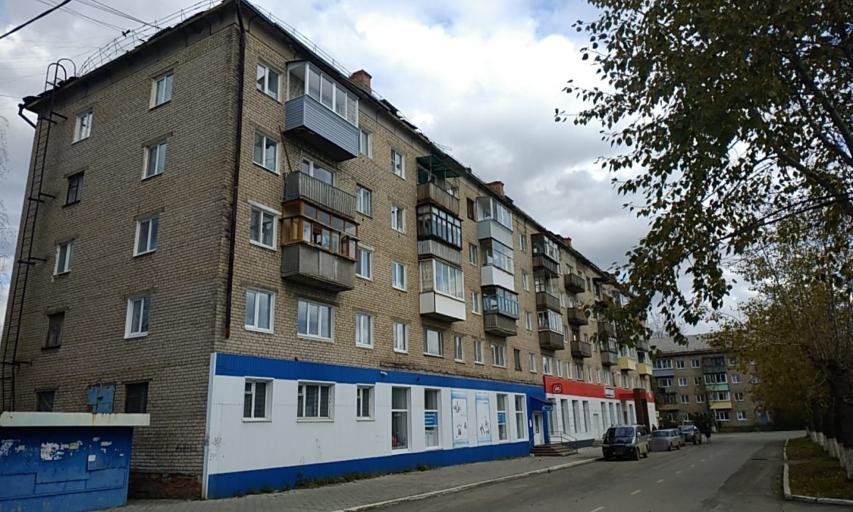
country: RU
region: Sverdlovsk
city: Krasnoural'sk
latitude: 58.3572
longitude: 60.0389
